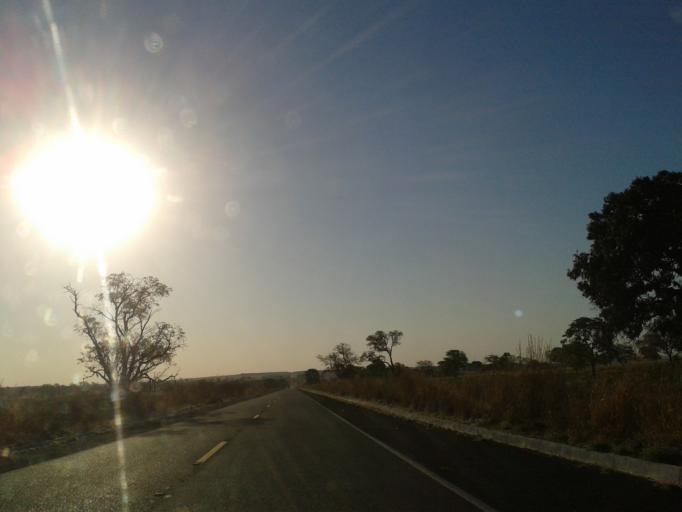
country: BR
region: Minas Gerais
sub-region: Santa Vitoria
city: Santa Vitoria
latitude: -19.0863
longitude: -50.3514
